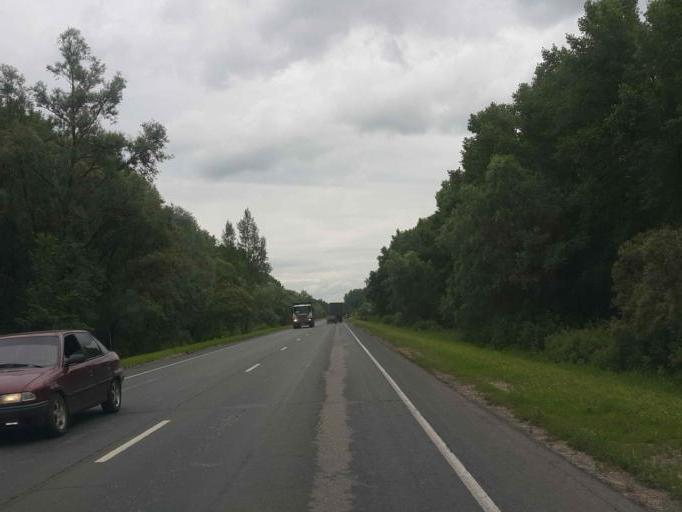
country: RU
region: Tambov
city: Zavoronezhskoye
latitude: 52.9445
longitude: 40.5926
